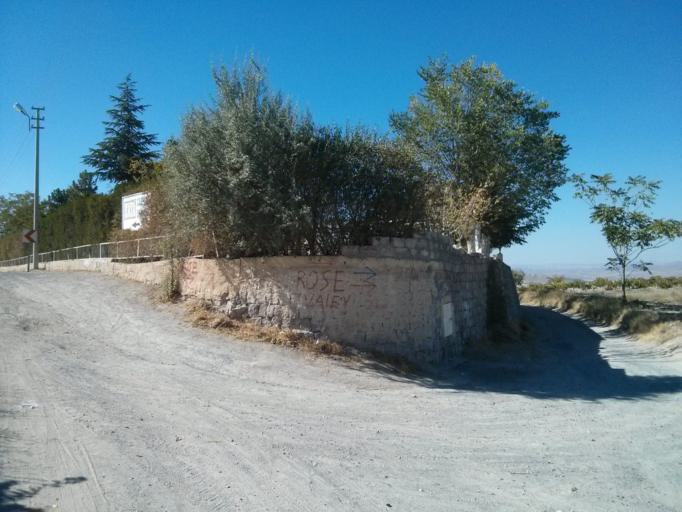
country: TR
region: Nevsehir
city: Goereme
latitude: 38.6366
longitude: 34.8552
